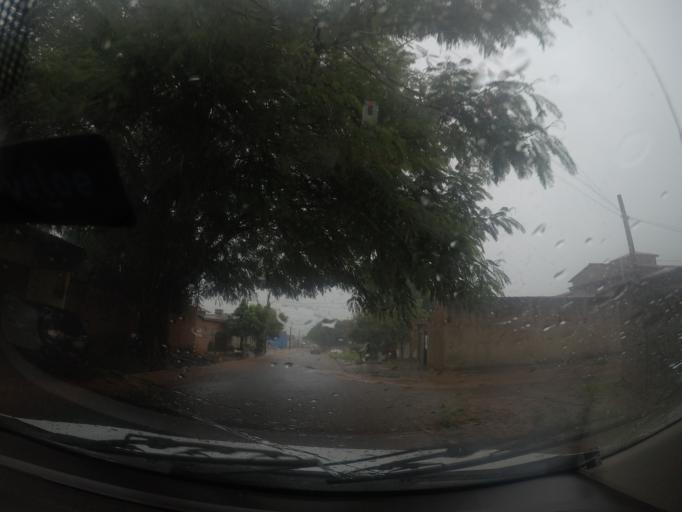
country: BR
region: Goias
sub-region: Goiania
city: Goiania
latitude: -16.6016
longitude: -49.3281
